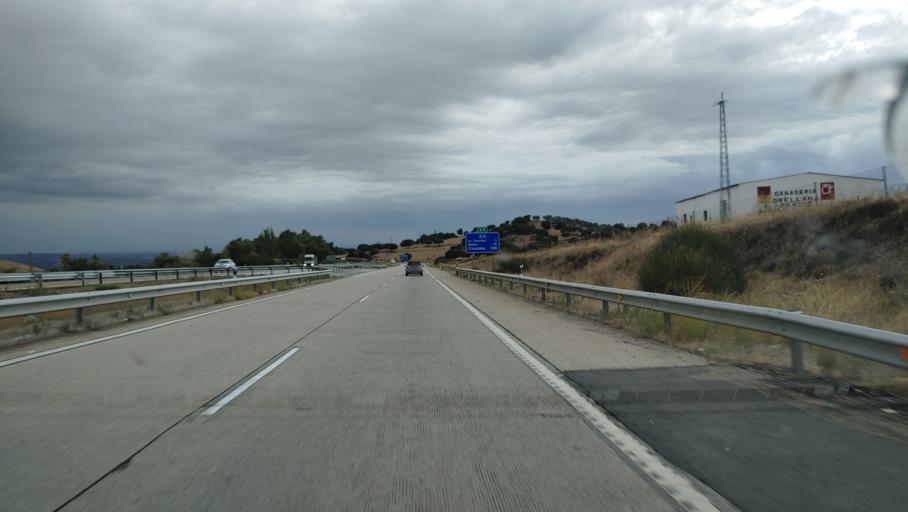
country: ES
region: Andalusia
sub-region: Provincia de Jaen
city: Santa Elena
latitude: 38.3117
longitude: -3.5741
